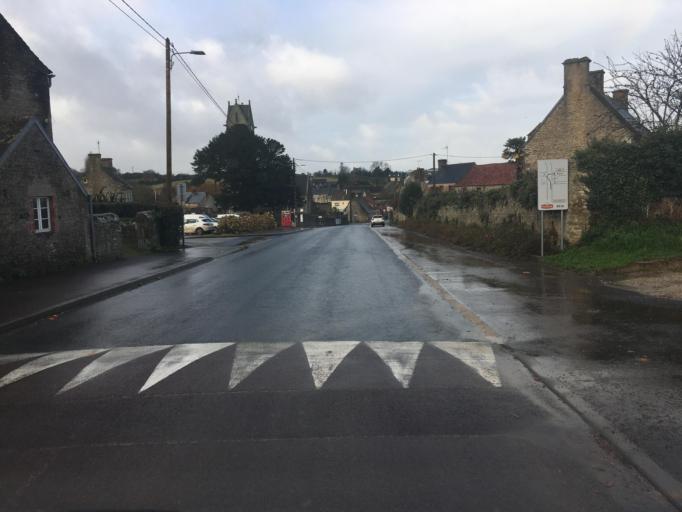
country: FR
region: Lower Normandy
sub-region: Departement de la Manche
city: Saint-Pierre-Eglise
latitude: 49.6707
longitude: -1.3347
